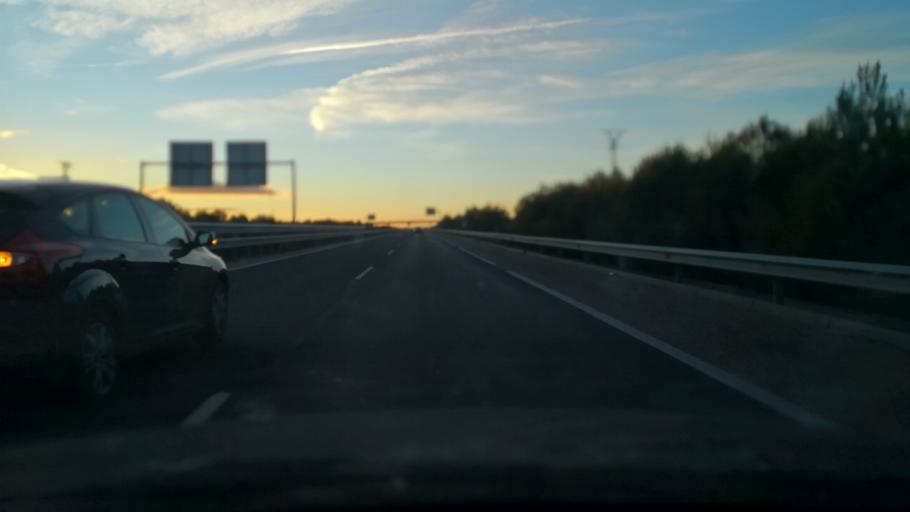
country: ES
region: Castille and Leon
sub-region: Provincia de Valladolid
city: Tordesillas
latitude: 41.5043
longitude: -5.0342
